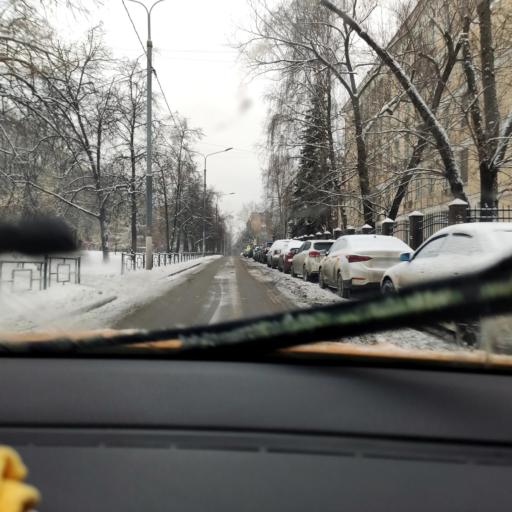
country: RU
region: Moscow
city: Tekstil'shchiki
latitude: 55.7041
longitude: 37.7367
